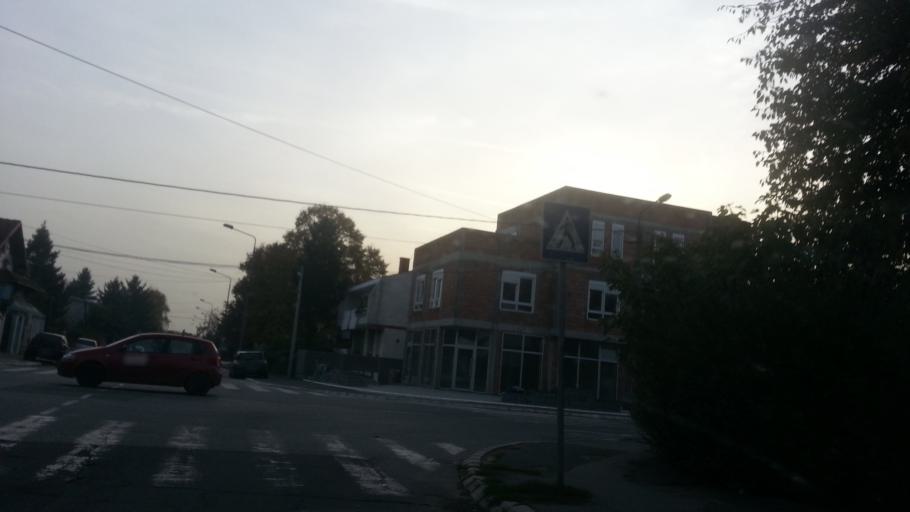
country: RS
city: Novi Banovci
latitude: 44.8977
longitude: 20.2841
